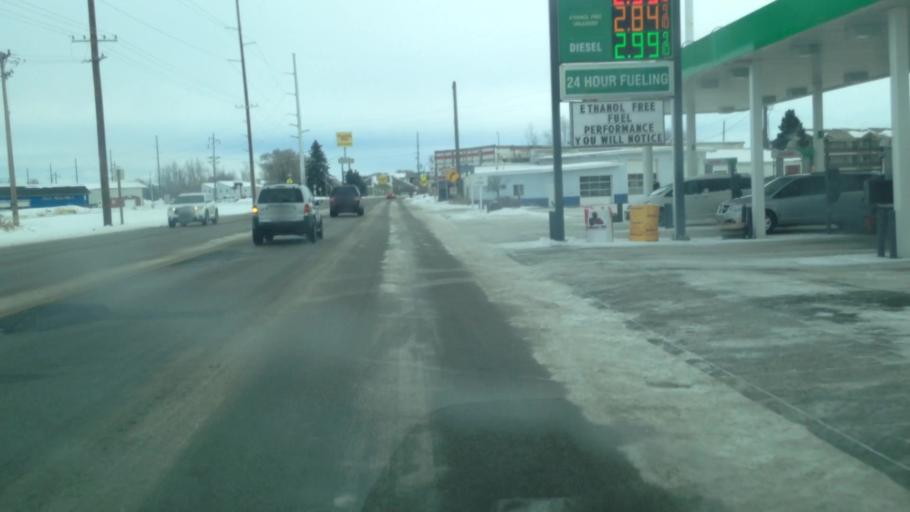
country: US
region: Idaho
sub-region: Madison County
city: Rexburg
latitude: 43.8156
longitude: -111.7993
